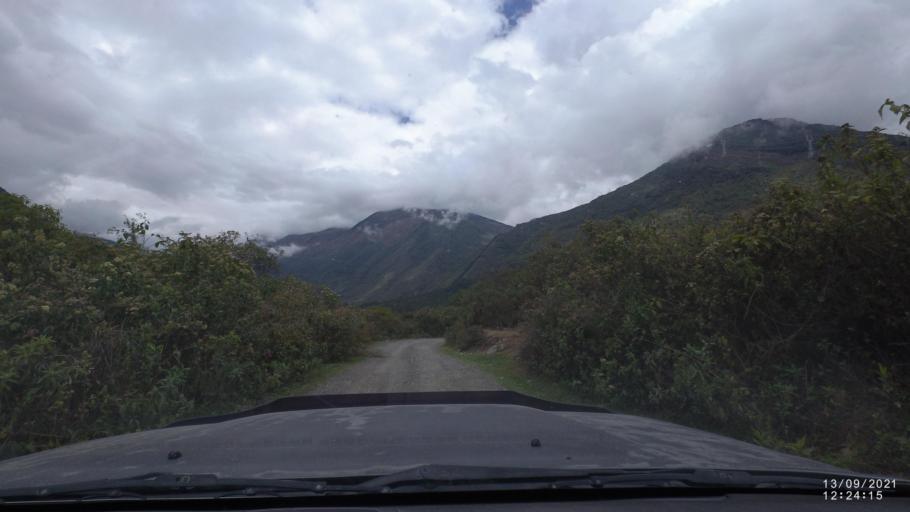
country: BO
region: Cochabamba
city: Colomi
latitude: -17.2457
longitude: -65.8182
